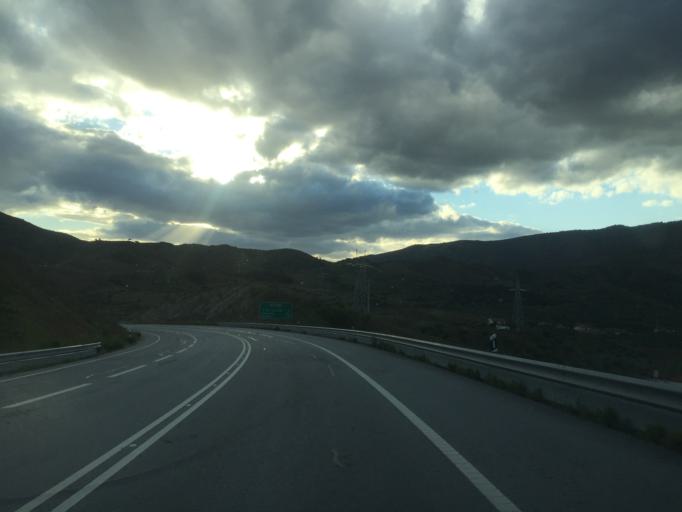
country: PT
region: Guarda
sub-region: Vila Nova de Foz Coa
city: Vila Nova de Foz Coa
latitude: 41.1270
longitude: -7.1272
